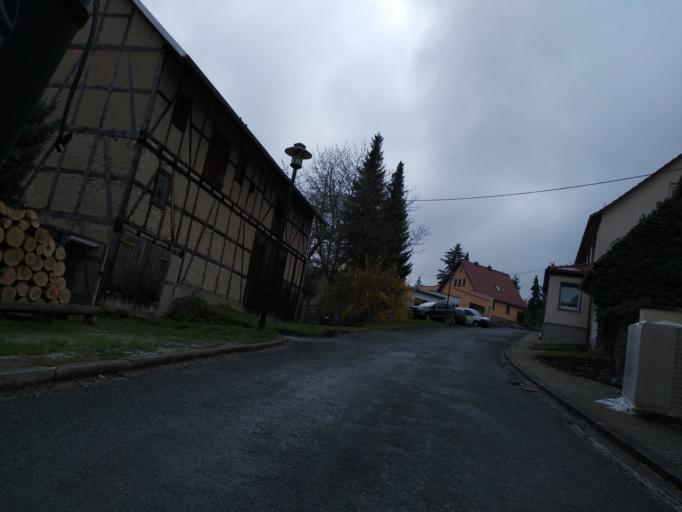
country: DE
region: Thuringia
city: Buchfart
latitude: 50.9199
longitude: 11.3320
